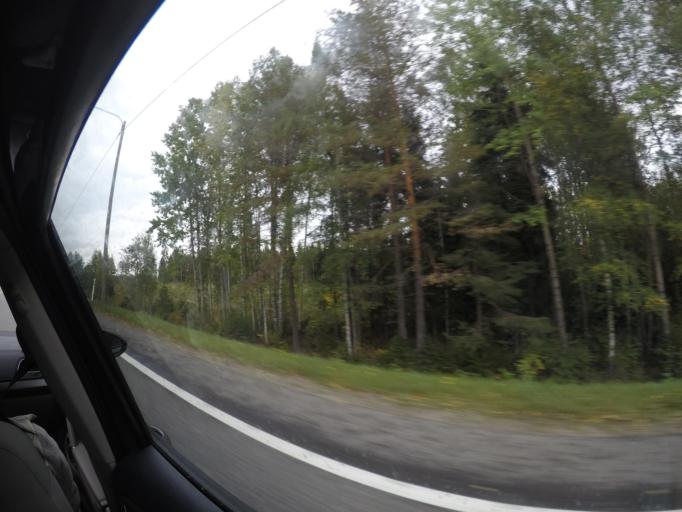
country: FI
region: Haeme
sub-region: Haemeenlinna
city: Parola
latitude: 61.1817
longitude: 24.4135
